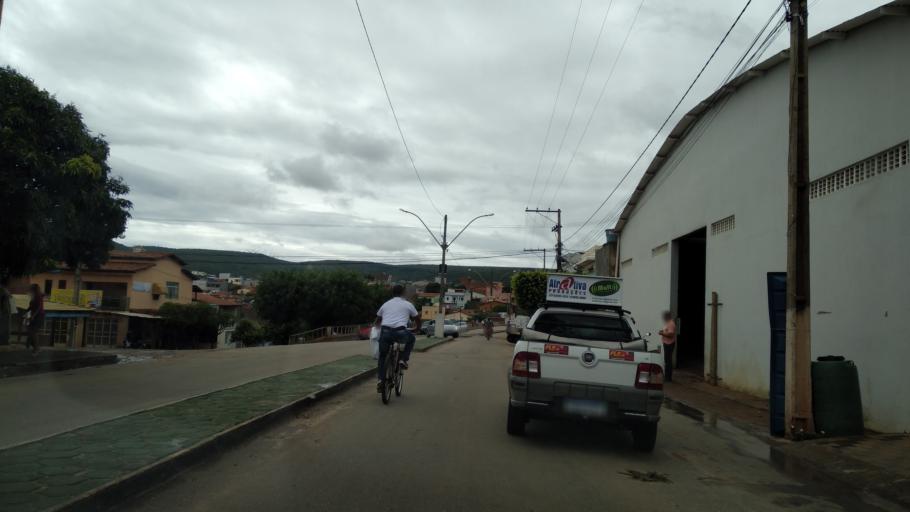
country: BR
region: Bahia
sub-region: Caetite
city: Caetite
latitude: -14.0605
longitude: -42.4839
